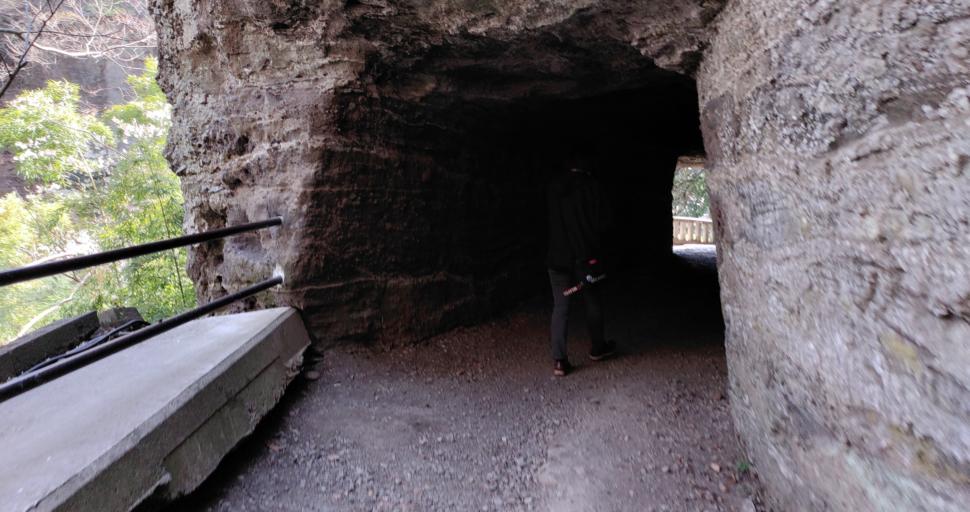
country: JP
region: Nagano
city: Komoro
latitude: 36.3312
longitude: 138.3861
